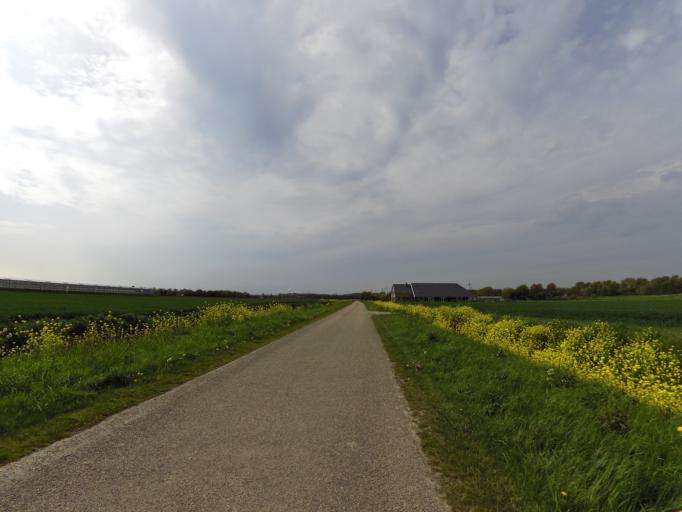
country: NL
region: South Holland
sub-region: Gemeente Brielle
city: Brielle
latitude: 51.9171
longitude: 4.1572
